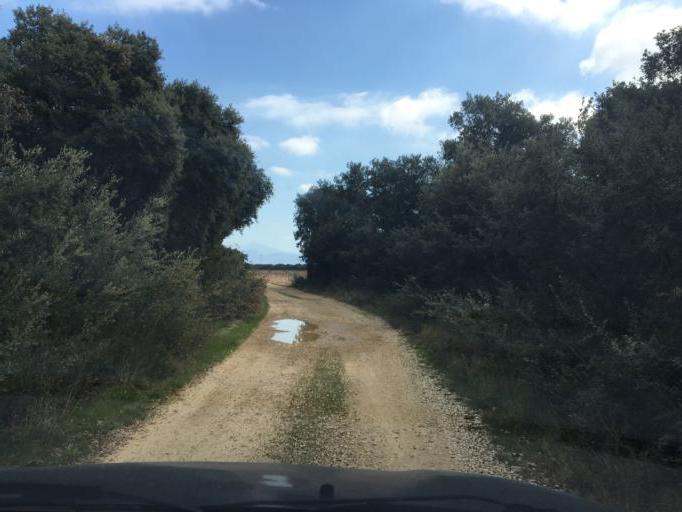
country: FR
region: Provence-Alpes-Cote d'Azur
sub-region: Departement du Vaucluse
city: Serignan-du-Comtat
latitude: 44.1846
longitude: 4.8608
